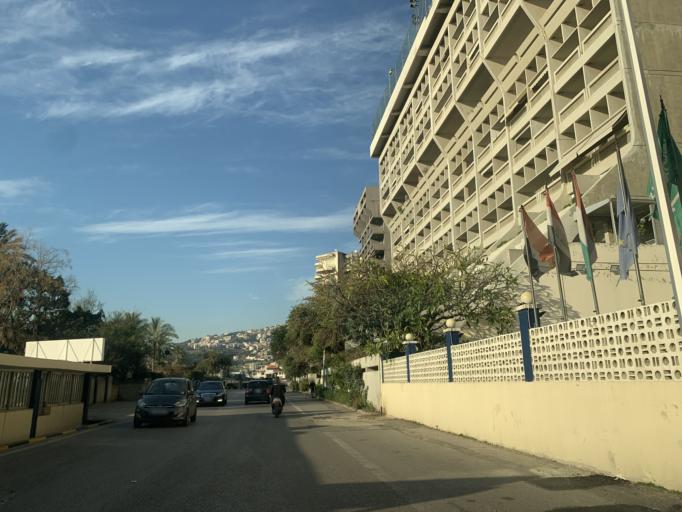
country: LB
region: Mont-Liban
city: Djounie
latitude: 33.9984
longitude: 35.6439
